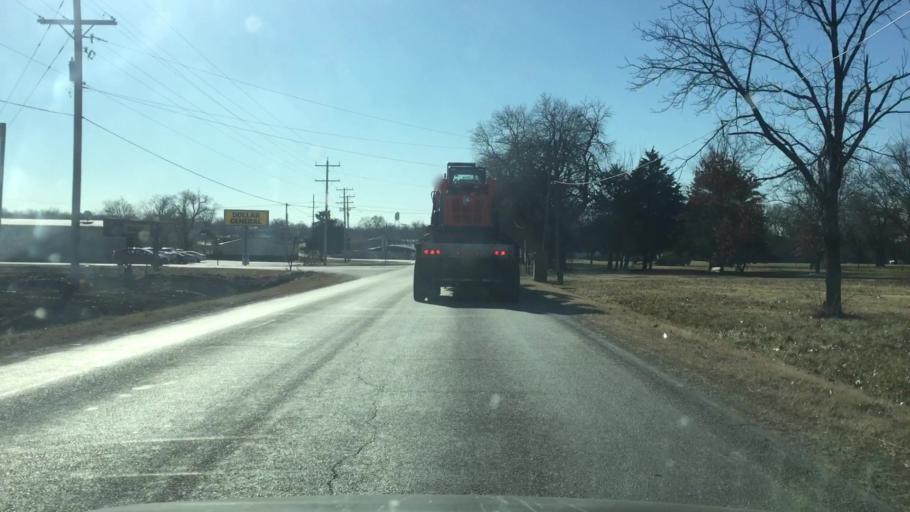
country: US
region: Kansas
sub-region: Allen County
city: Humboldt
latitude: 37.8226
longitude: -95.4368
